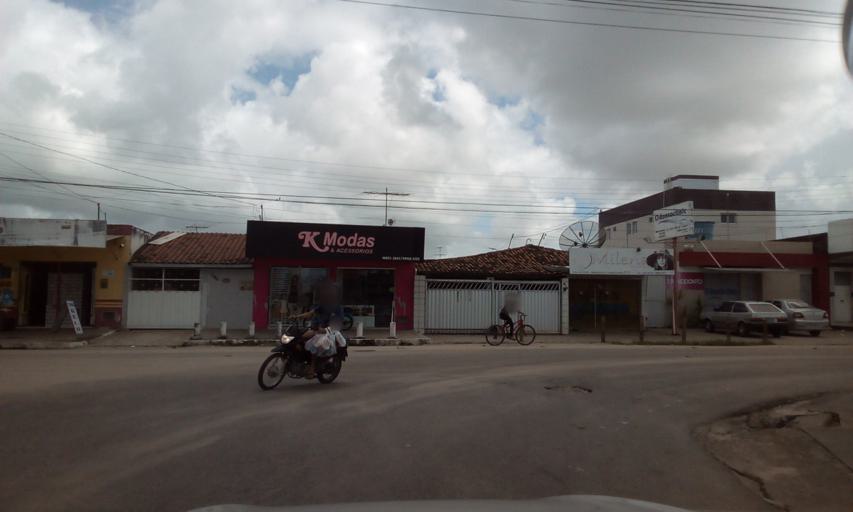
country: BR
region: Paraiba
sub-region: Conde
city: Conde
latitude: -7.2063
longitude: -34.8466
